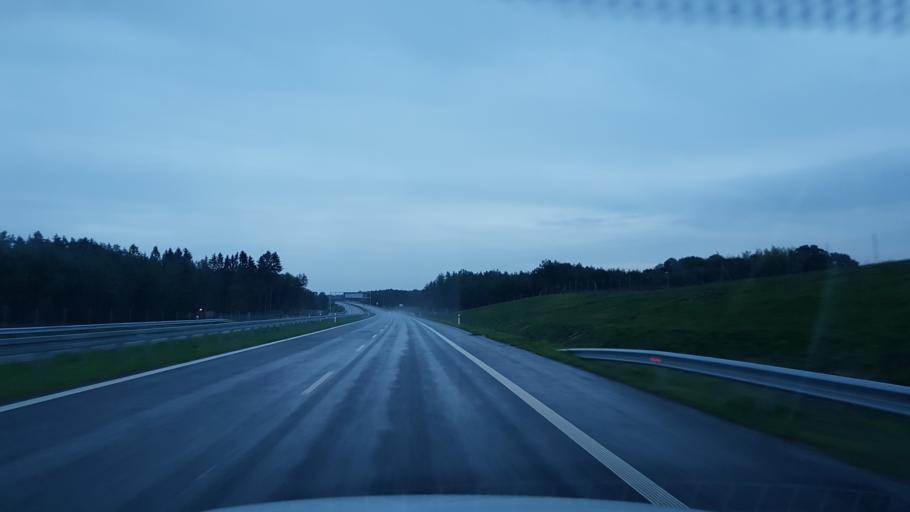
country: PL
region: West Pomeranian Voivodeship
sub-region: Powiat gryficki
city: Brojce
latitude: 53.9511
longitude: 15.4091
